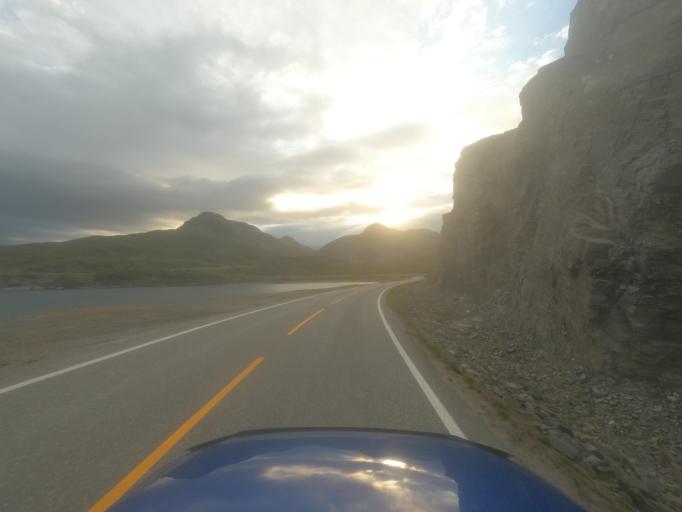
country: NO
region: Finnmark Fylke
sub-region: Nordkapp
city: Honningsvag
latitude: 70.6466
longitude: 25.3800
